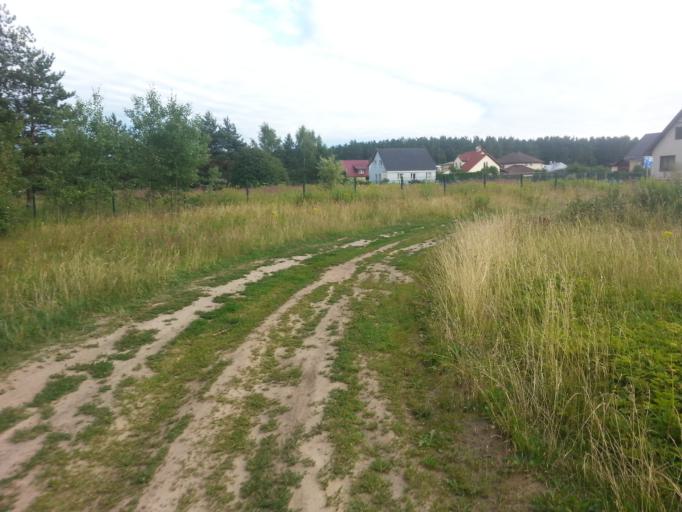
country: LV
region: Stopini
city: Ulbroka
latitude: 56.9492
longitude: 24.2629
